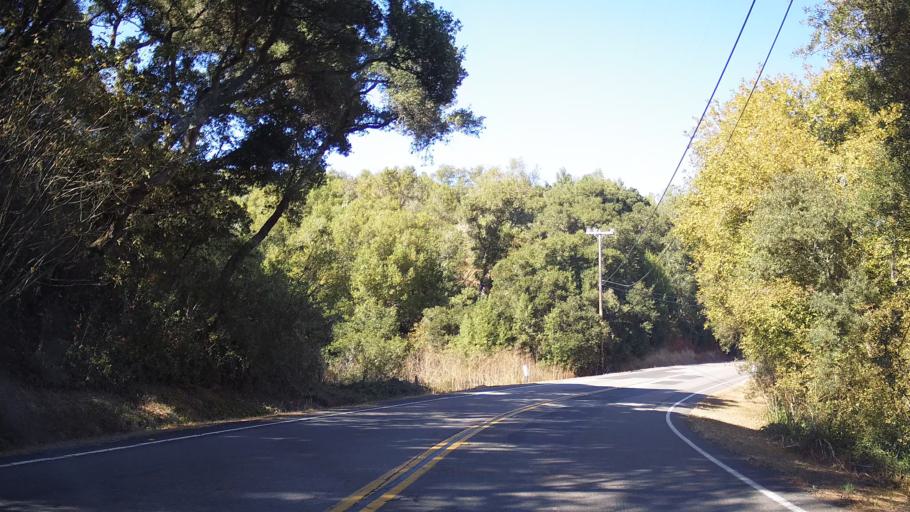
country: US
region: California
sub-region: Marin County
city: Inverness
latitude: 38.0809
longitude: -122.7849
